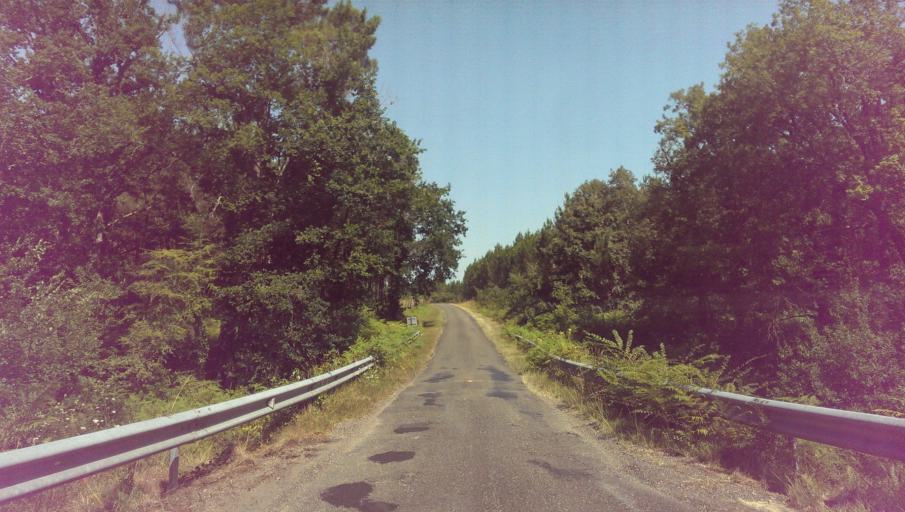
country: FR
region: Aquitaine
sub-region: Departement des Landes
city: Sarbazan
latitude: 44.0827
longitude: -0.1557
